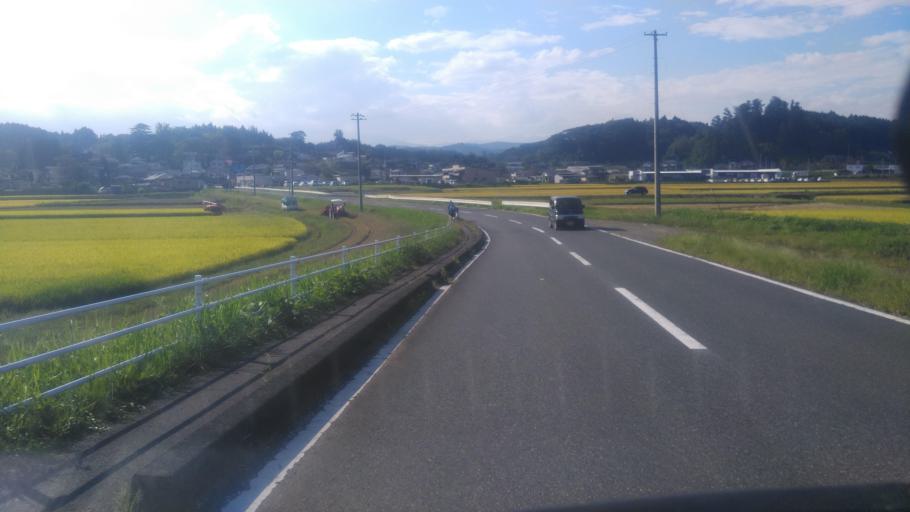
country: JP
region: Miyagi
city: Okawara
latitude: 38.1043
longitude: 140.6835
